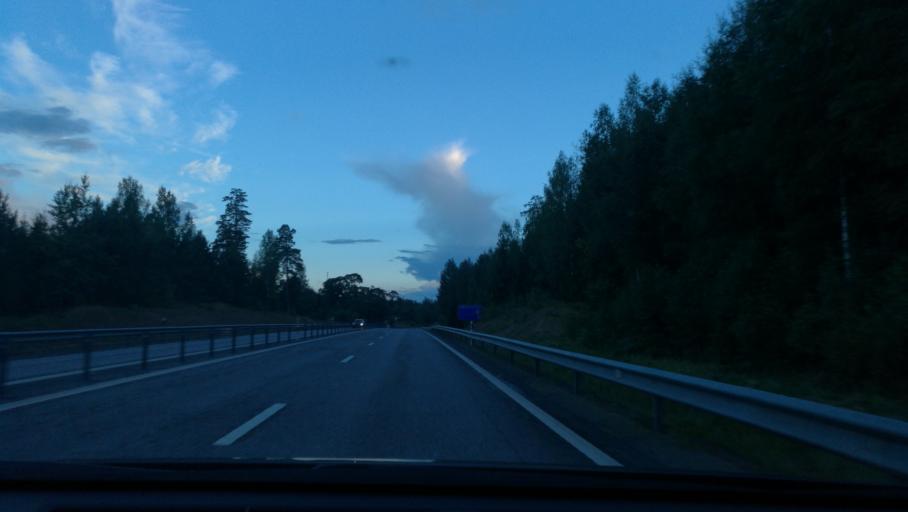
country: SE
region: Soedermanland
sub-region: Katrineholms Kommun
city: Katrineholm
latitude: 58.8485
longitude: 16.2040
